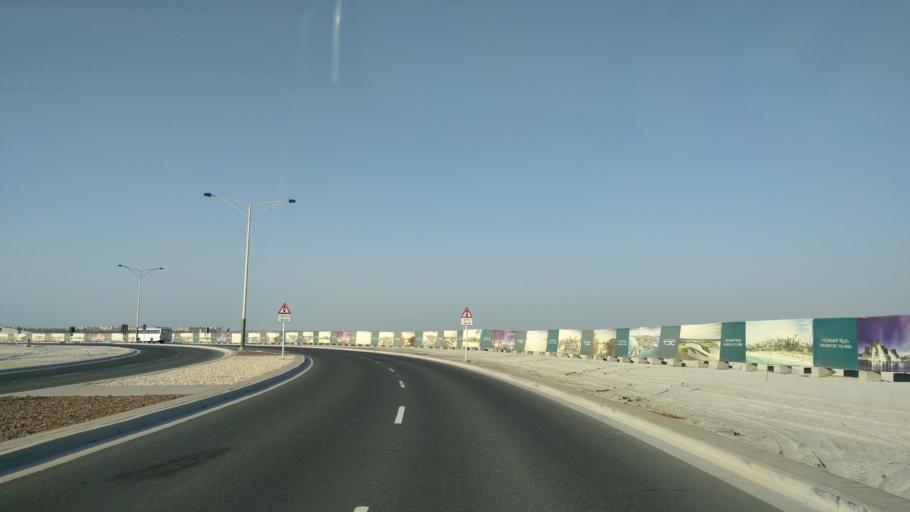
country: AE
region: Abu Dhabi
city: Abu Dhabi
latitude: 24.5313
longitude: 54.4385
